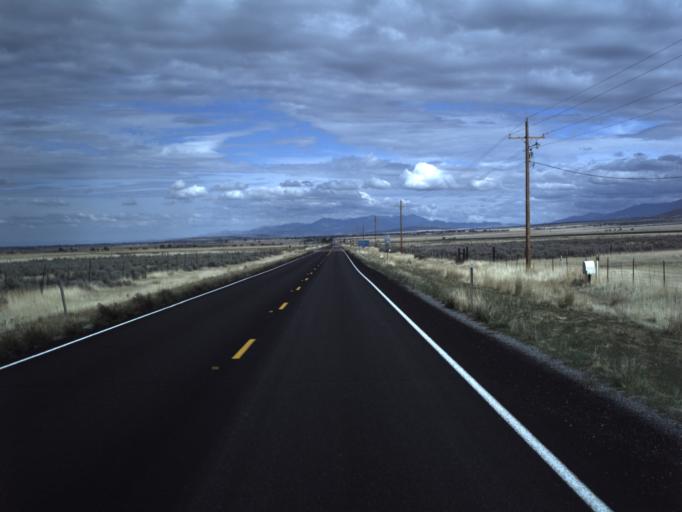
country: US
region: Utah
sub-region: Millard County
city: Fillmore
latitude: 38.8159
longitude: -112.4354
